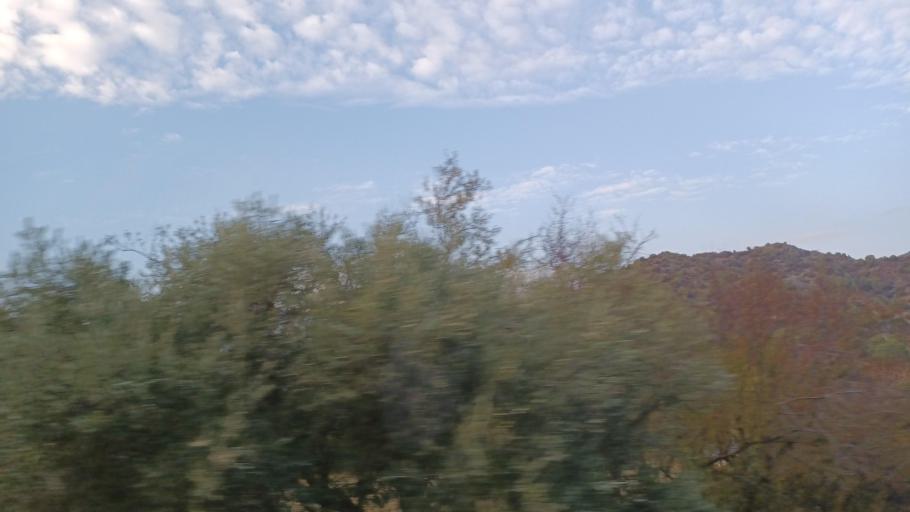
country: CY
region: Limassol
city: Pelendri
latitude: 34.8576
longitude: 32.9328
